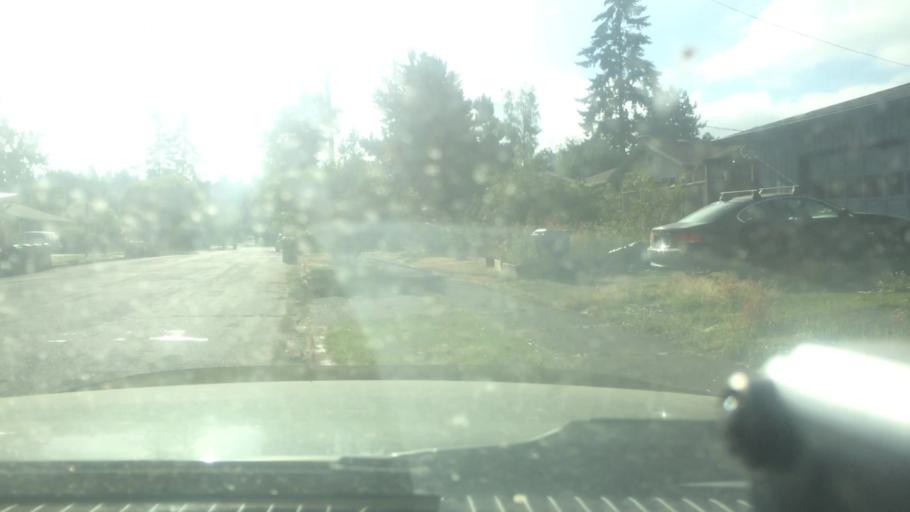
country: US
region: Oregon
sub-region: Lane County
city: Eugene
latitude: 44.0297
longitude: -123.1111
